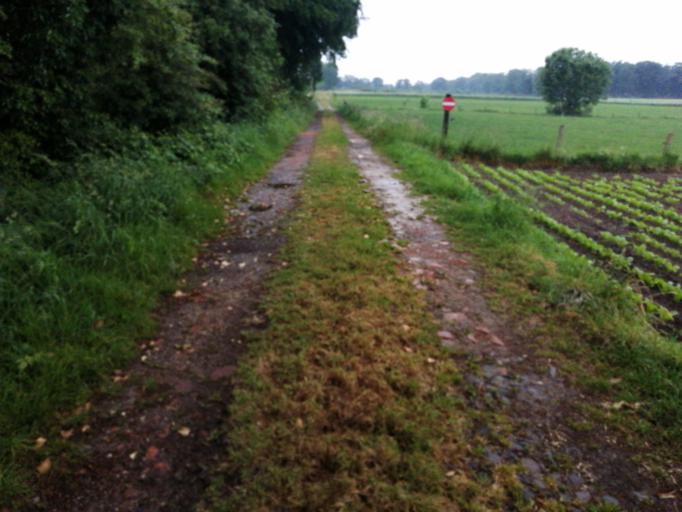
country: BE
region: Flanders
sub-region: Provincie West-Vlaanderen
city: Houthulst
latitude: 50.9503
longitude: 2.9380
